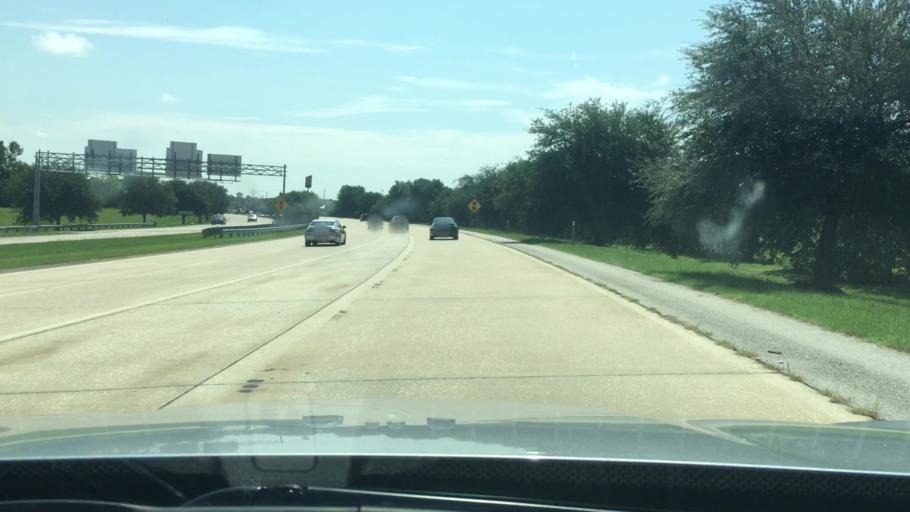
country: US
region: South Carolina
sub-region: Florence County
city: Florence
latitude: 34.1910
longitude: -79.8409
